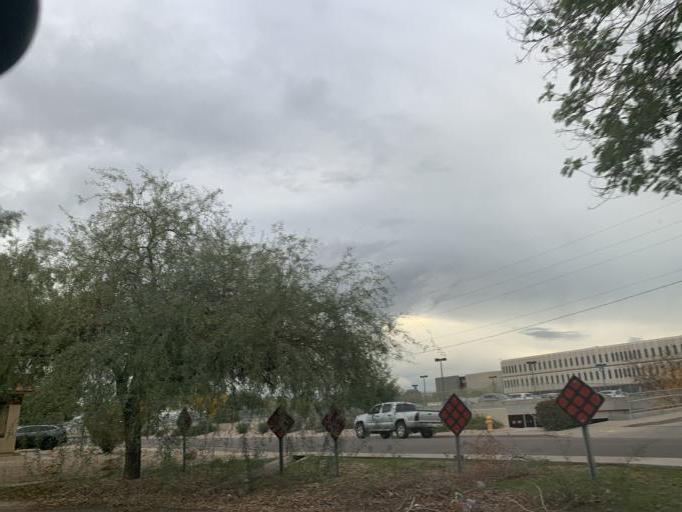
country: US
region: Arizona
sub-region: Maricopa County
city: Phoenix
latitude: 33.4648
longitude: -112.0541
